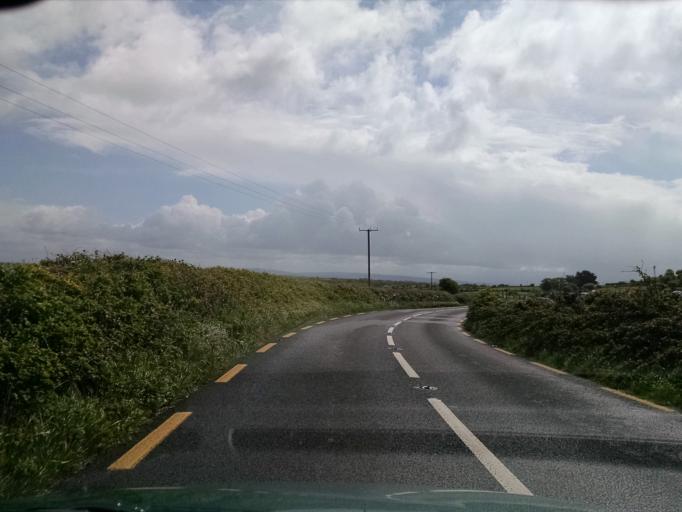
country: IE
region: Connaught
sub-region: County Galway
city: Gaillimh
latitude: 53.1452
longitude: -9.0363
